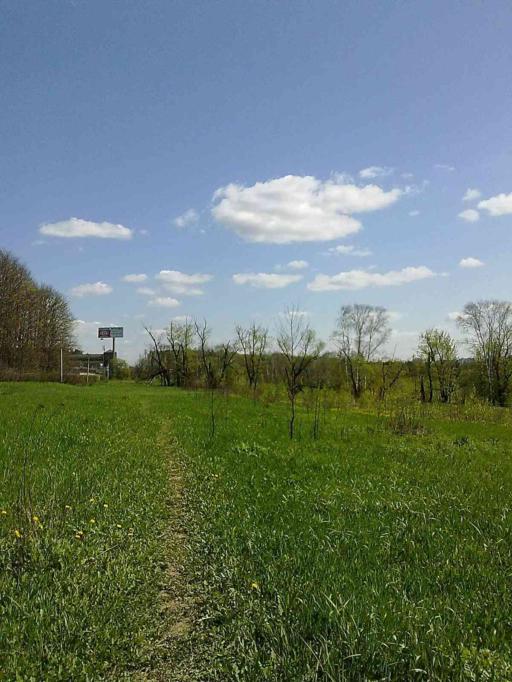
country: RU
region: Moscow
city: Yasenevo
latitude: 55.5883
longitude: 37.5392
